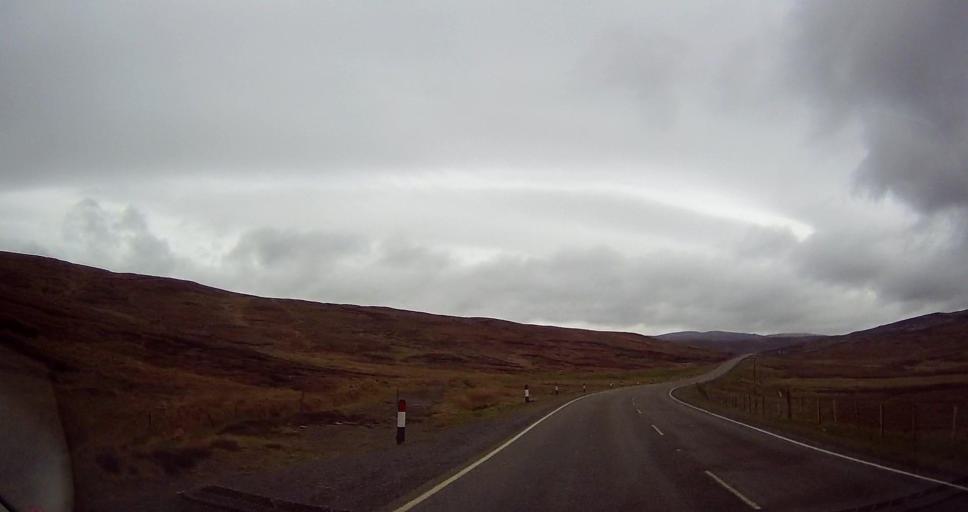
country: GB
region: Scotland
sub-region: Shetland Islands
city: Lerwick
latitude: 60.2675
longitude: -1.2297
